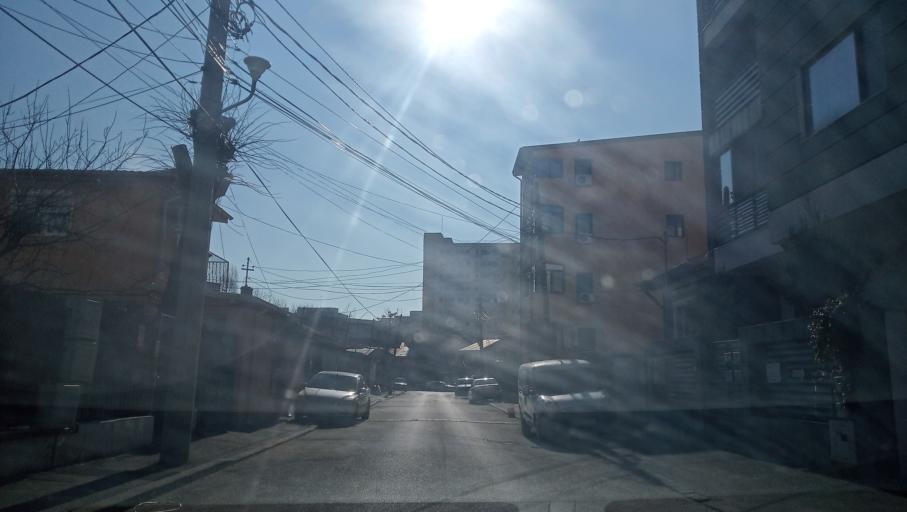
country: RO
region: Ilfov
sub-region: Comuna Fundeni-Dobroesti
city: Fundeni
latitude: 44.4403
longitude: 26.1590
